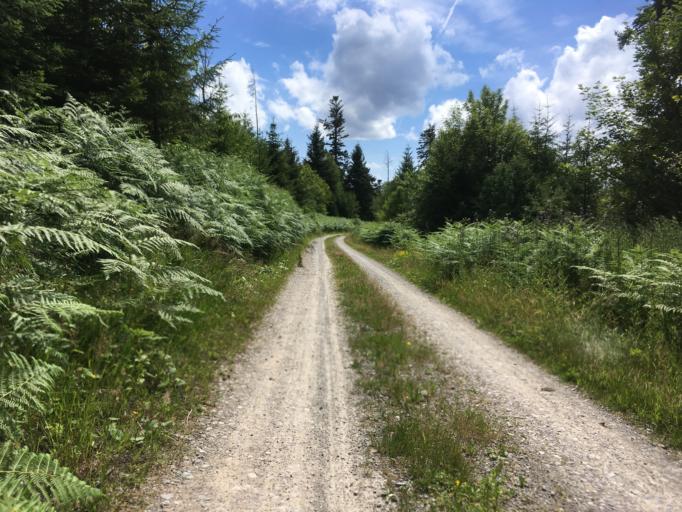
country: DE
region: Baden-Wuerttemberg
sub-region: Karlsruhe Region
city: Baiersbronn
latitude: 48.5698
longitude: 8.4185
